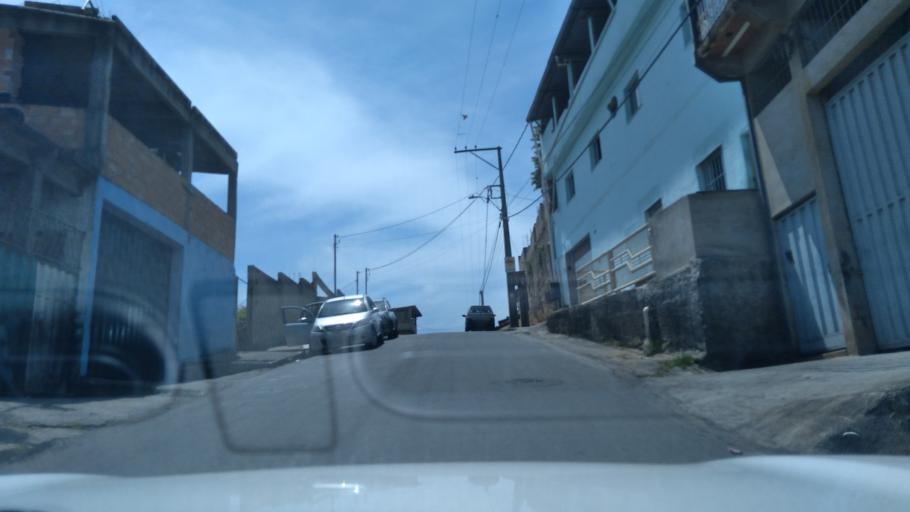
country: BR
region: Minas Gerais
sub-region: Contagem
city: Contagem
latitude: -19.9175
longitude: -44.0236
